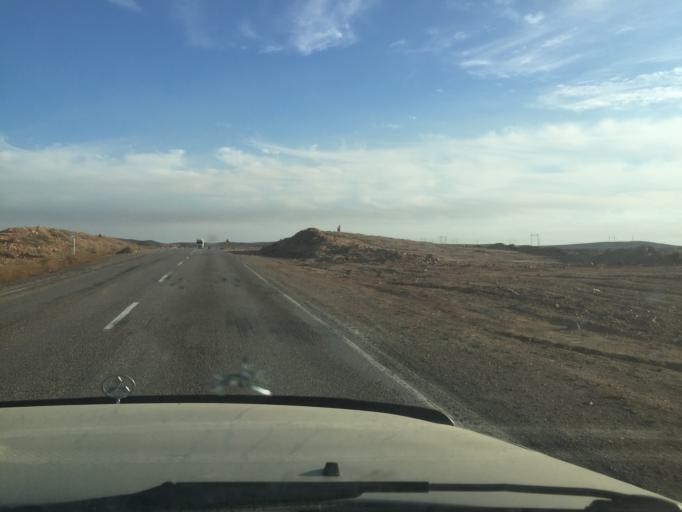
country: KZ
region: Zhambyl
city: Mynaral
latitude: 45.5226
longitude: 73.4868
